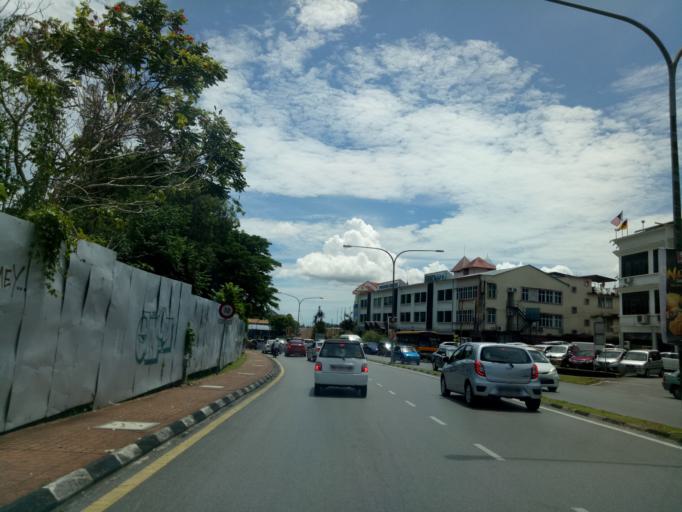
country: MY
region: Sarawak
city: Kuching
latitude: 1.5537
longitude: 110.3484
